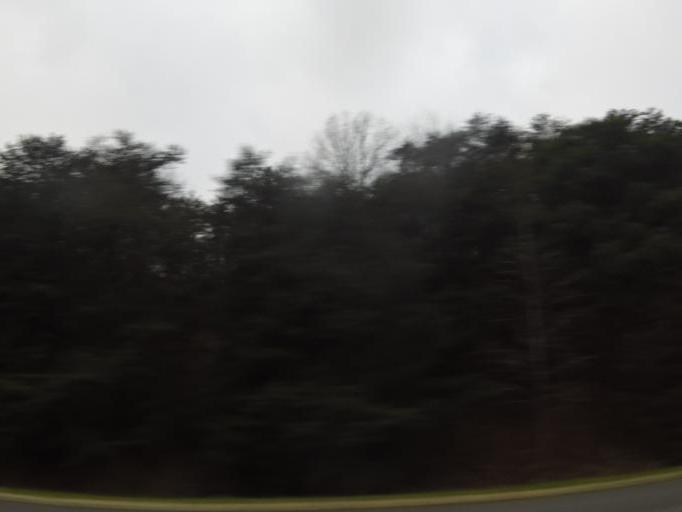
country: US
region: Alabama
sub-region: Jefferson County
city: Morris
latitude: 33.7366
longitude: -86.8256
